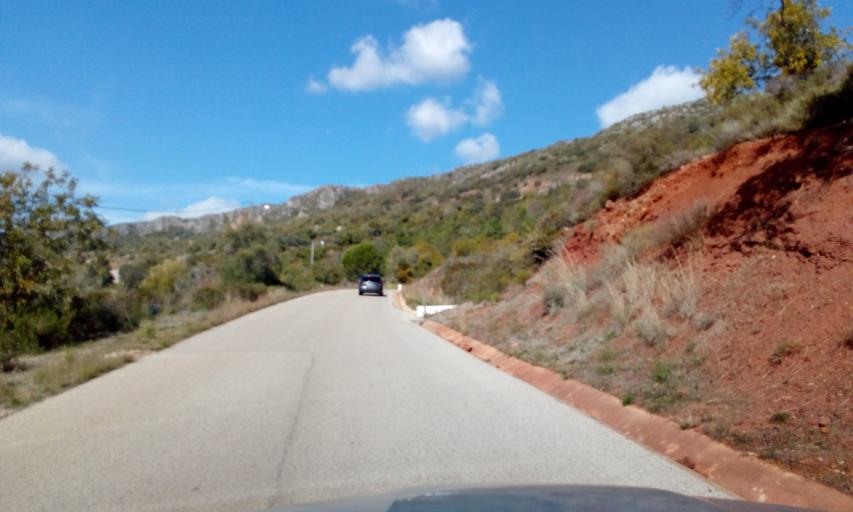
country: PT
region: Faro
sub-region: Loule
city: Boliqueime
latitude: 37.2487
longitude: -8.0911
